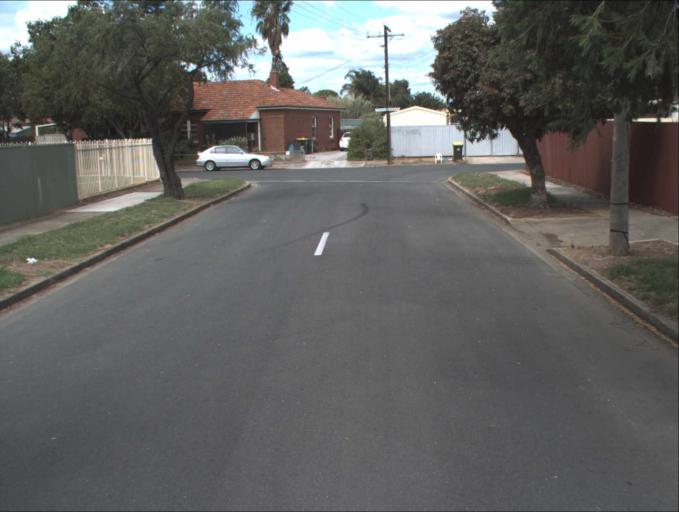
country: AU
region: South Australia
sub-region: Port Adelaide Enfield
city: Blair Athol
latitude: -34.8588
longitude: 138.5800
